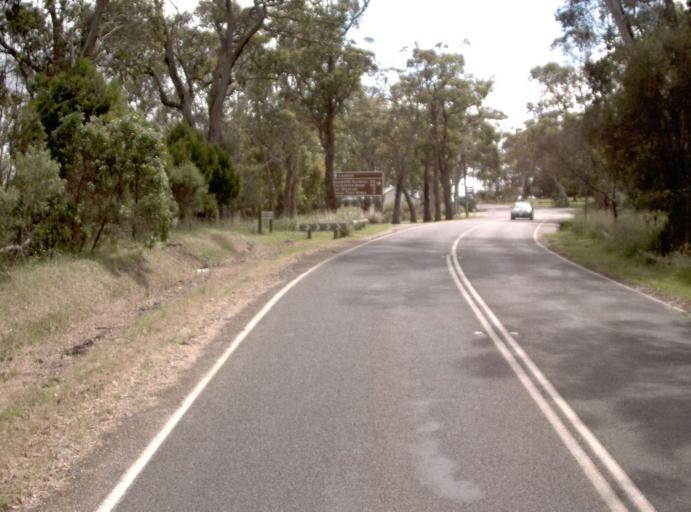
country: AU
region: Victoria
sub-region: Mornington Peninsula
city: McCrae
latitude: -38.3549
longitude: 144.9489
